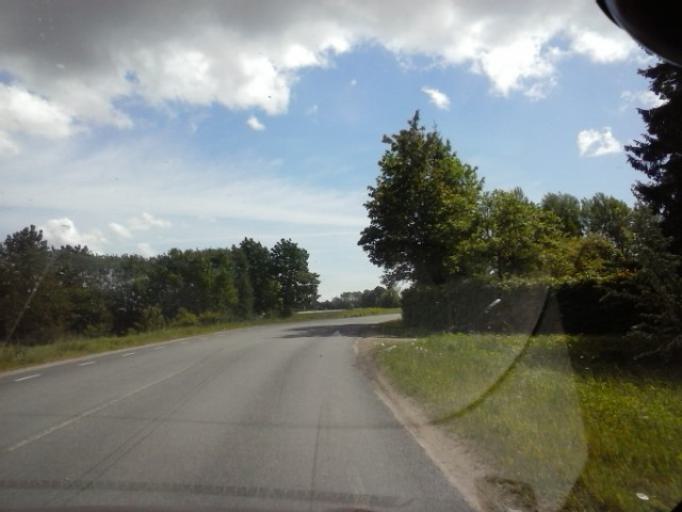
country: EE
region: Laeaene
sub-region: Ridala Parish
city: Uuemoisa
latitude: 58.9621
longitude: 23.7833
